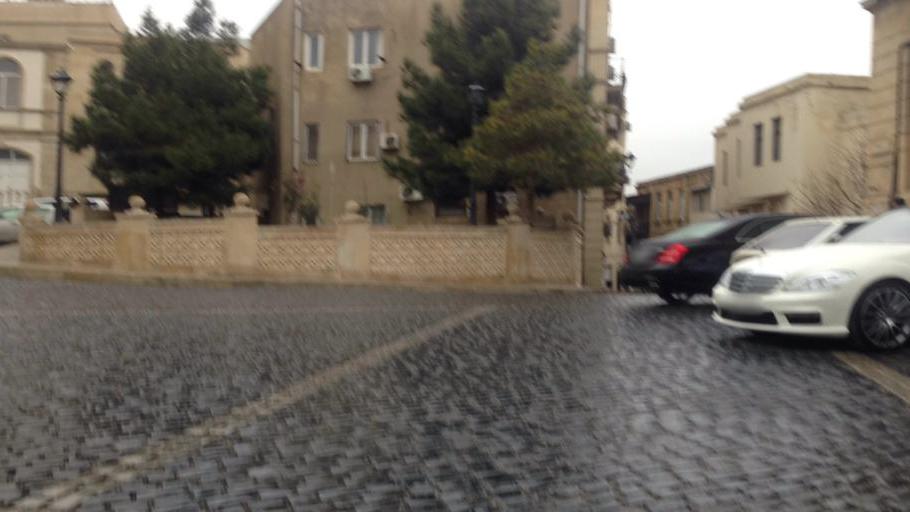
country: AZ
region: Baki
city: Badamdar
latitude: 40.3667
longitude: 49.8362
